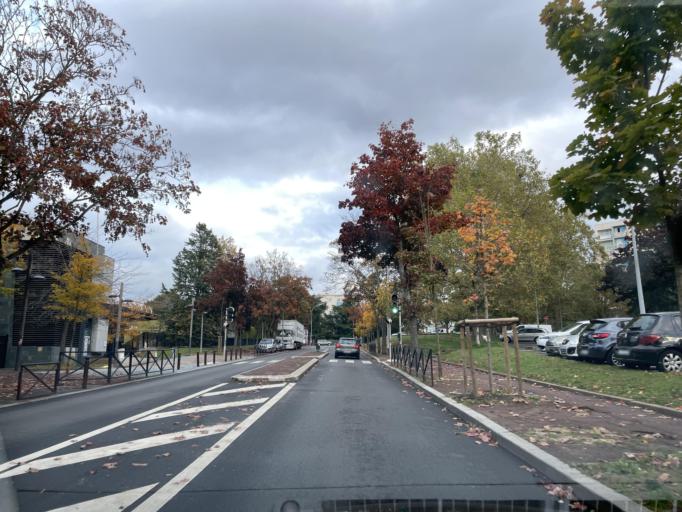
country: FR
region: Ile-de-France
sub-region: Departement du Val-de-Marne
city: Creteil
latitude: 48.7827
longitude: 2.4623
